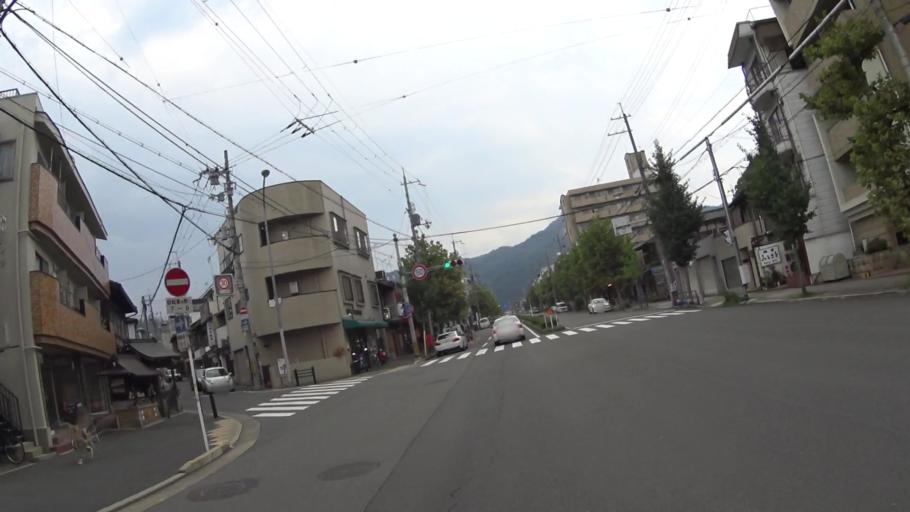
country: JP
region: Kyoto
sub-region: Kyoto-shi
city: Kamigyo-ku
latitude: 35.0288
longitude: 135.7870
